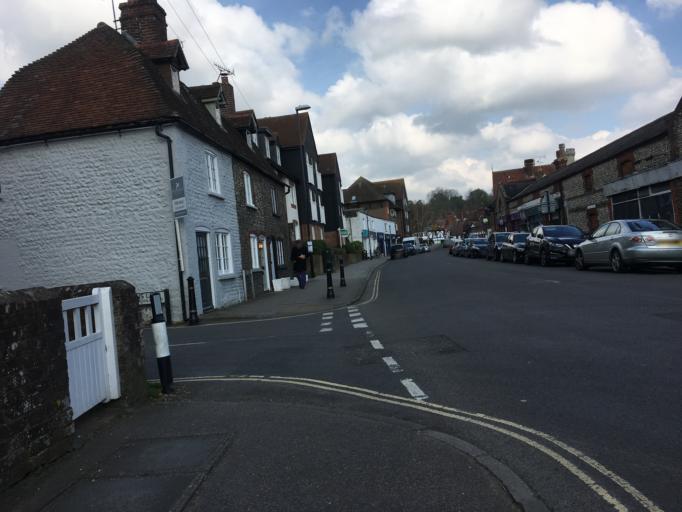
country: GB
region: England
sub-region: West Sussex
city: Arundel
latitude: 50.8524
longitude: -0.5516
